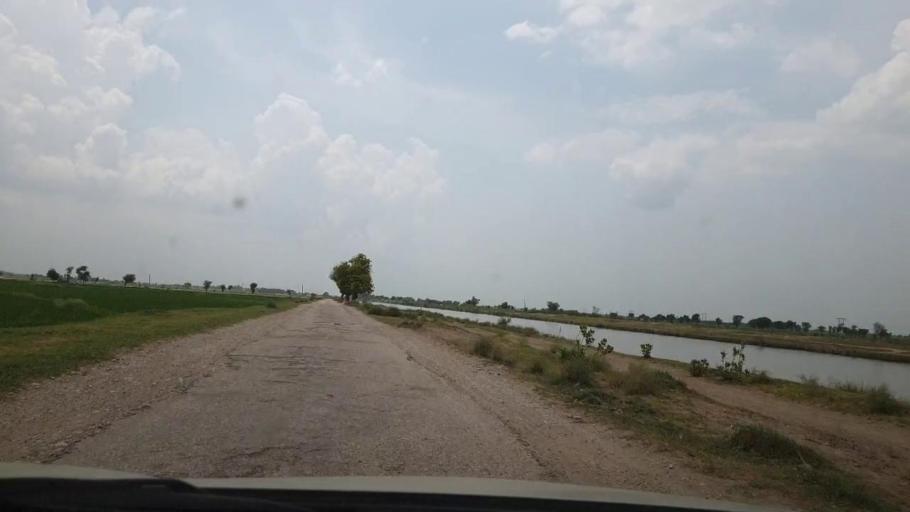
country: PK
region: Sindh
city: Goth Garelo
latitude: 27.4312
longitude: 68.1084
